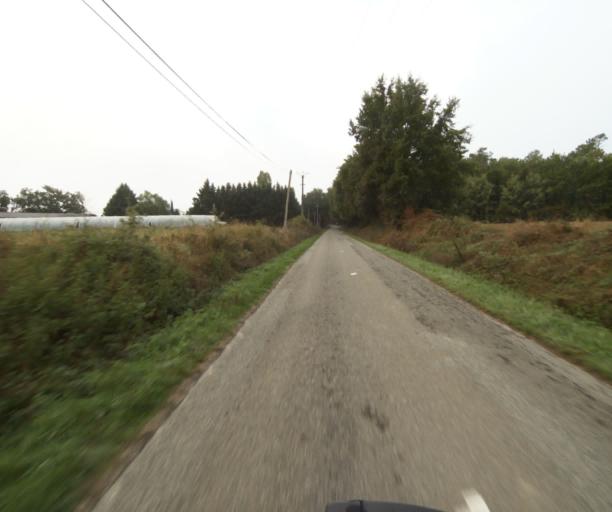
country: FR
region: Midi-Pyrenees
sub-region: Departement du Tarn-et-Garonne
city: Saint-Nauphary
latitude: 43.9425
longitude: 1.4417
